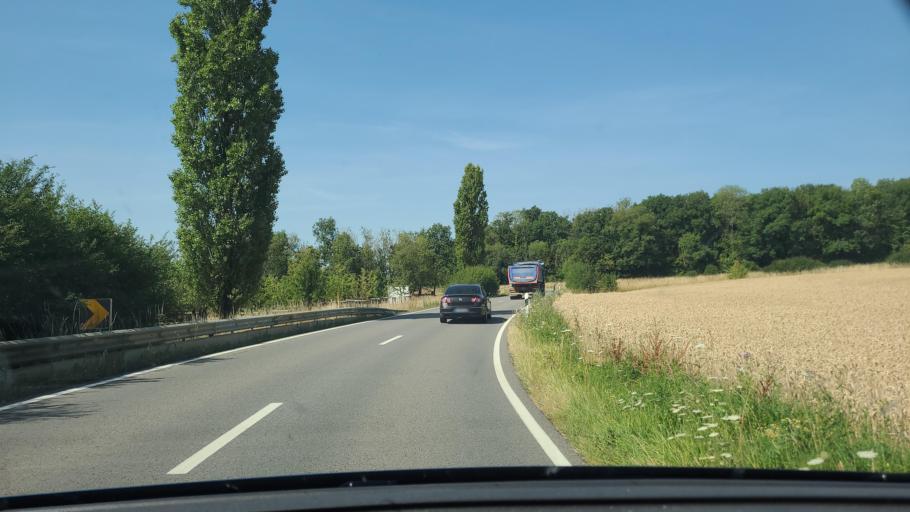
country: LU
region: Luxembourg
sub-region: Canton d'Esch-sur-Alzette
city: Mondercange
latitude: 49.5501
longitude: 5.9682
